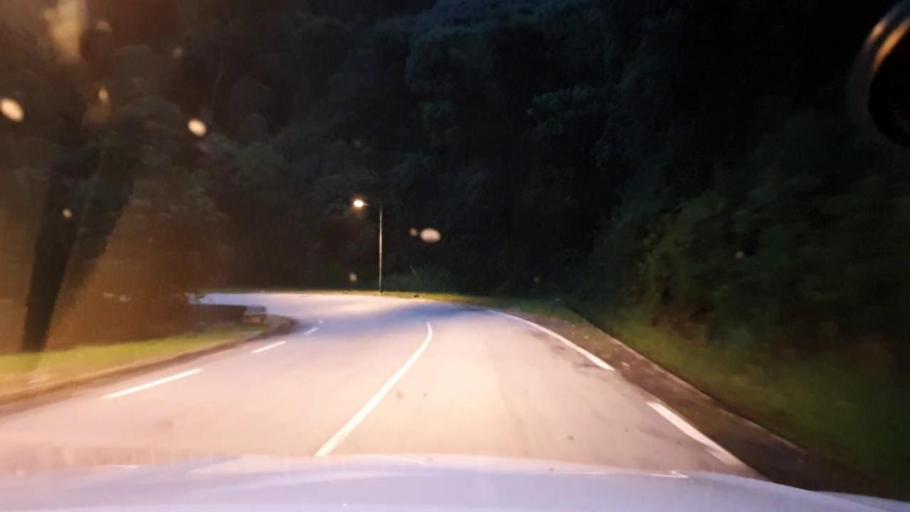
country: RW
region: Southern Province
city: Nzega
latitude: -2.5312
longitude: 29.3844
